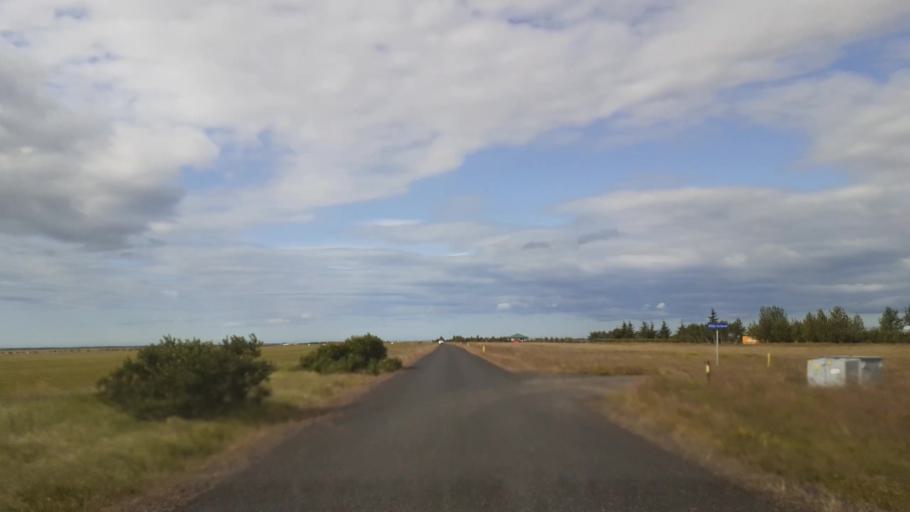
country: IS
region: South
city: Vestmannaeyjar
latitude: 63.7708
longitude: -20.2854
